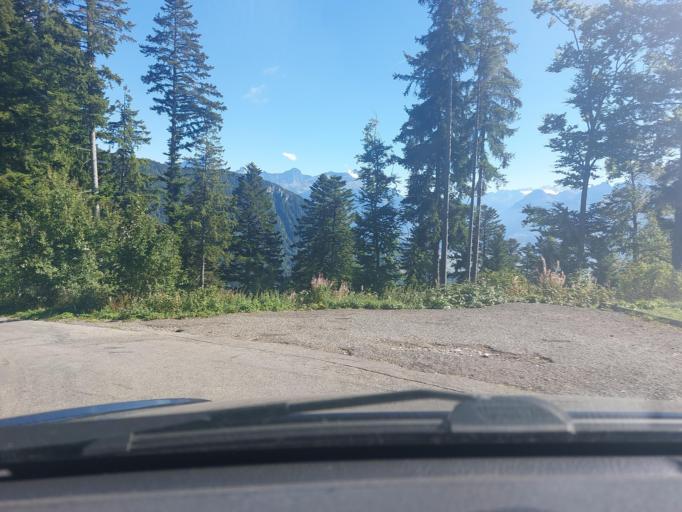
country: CH
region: Vaud
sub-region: Aigle District
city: Aigle
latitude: 46.3586
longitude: 6.9601
